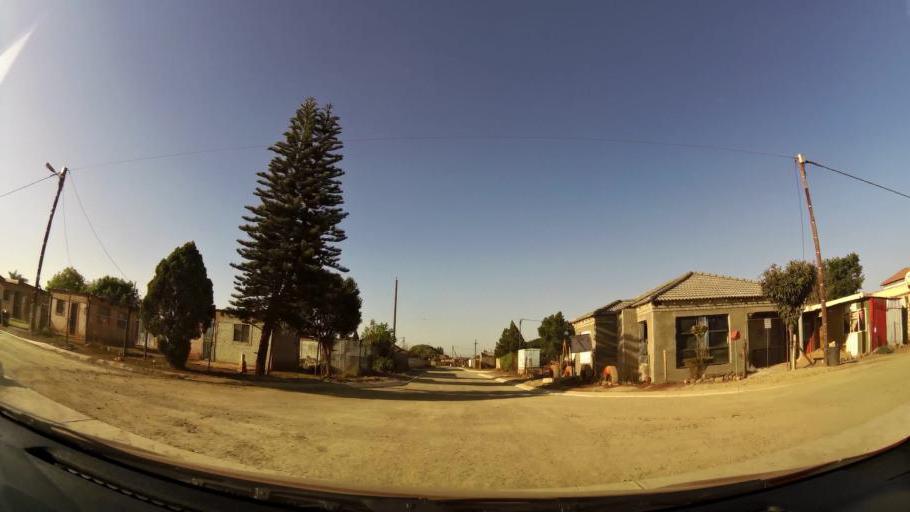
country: ZA
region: Gauteng
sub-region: City of Tshwane Metropolitan Municipality
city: Mabopane
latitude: -25.5921
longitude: 28.0999
